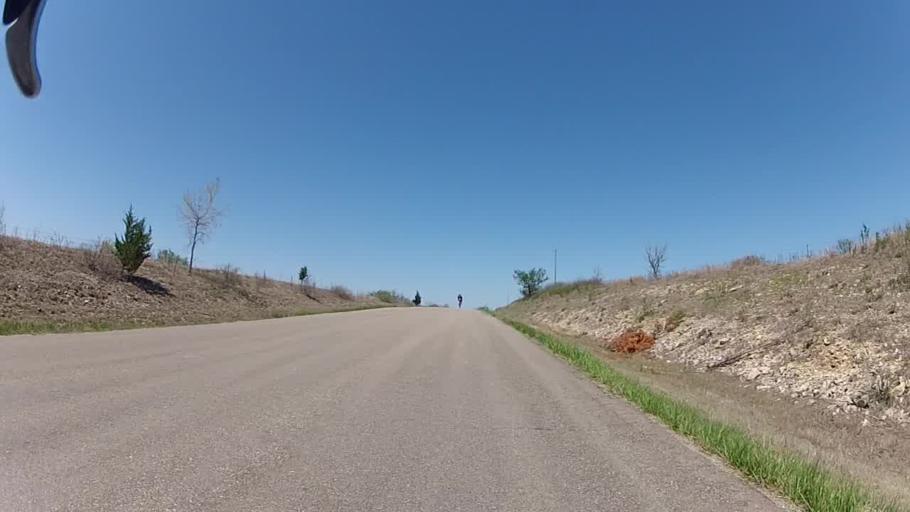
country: US
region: Kansas
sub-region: Riley County
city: Ogden
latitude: 38.9717
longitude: -96.5444
